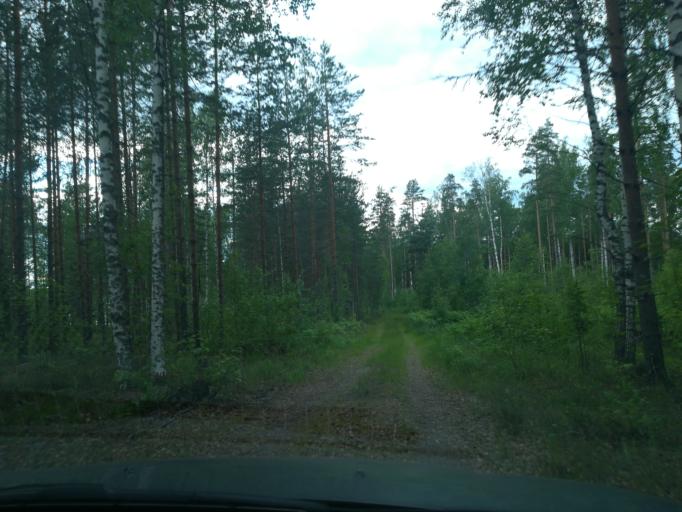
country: FI
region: South Karelia
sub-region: Lappeenranta
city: Savitaipale
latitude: 61.5018
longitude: 27.8386
